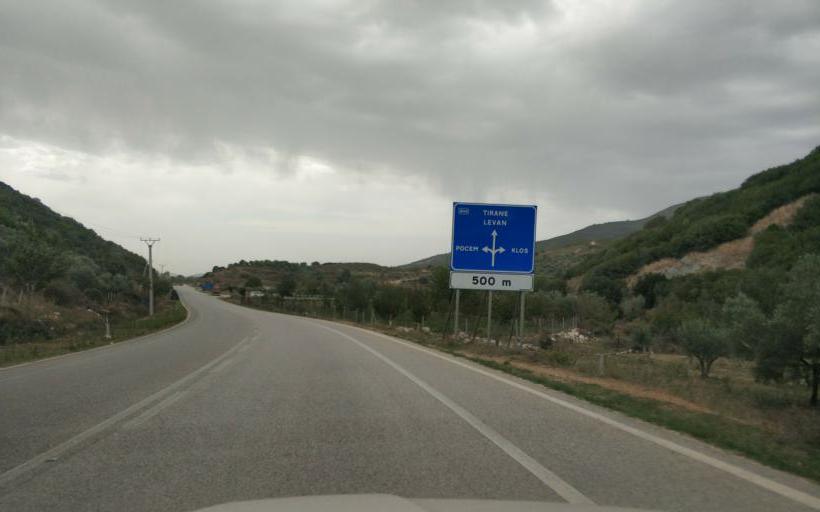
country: AL
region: Fier
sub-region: Rrethi i Mallakastres
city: Kute
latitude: 40.5124
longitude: 19.7508
